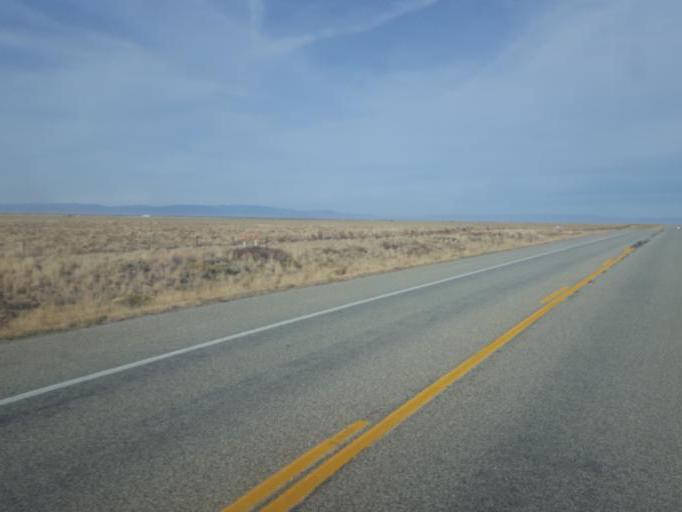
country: US
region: Colorado
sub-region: Alamosa County
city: Alamosa East
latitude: 37.4633
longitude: -105.5644
